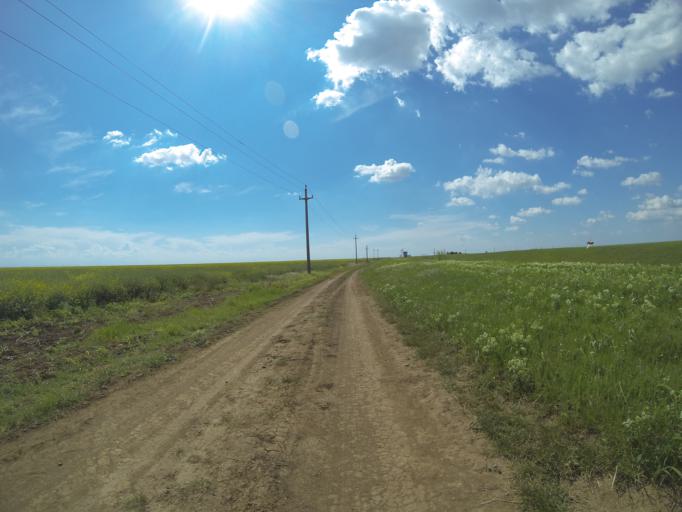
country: RO
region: Dolj
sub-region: Comuna Segarcea
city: Segarcea
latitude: 44.0199
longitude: 23.7534
